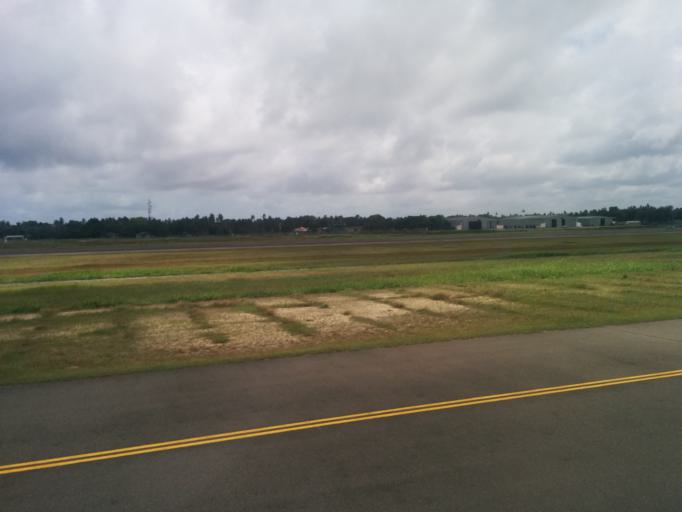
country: LK
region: Western
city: Katunayaka
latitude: 7.1760
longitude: 79.8820
